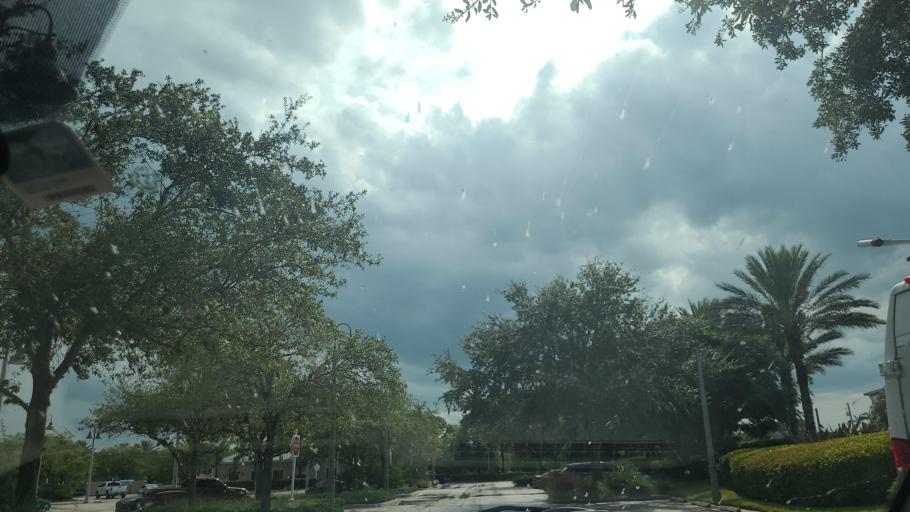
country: US
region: Florida
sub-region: Martin County
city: North River Shores
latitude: 27.2109
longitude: -80.3268
